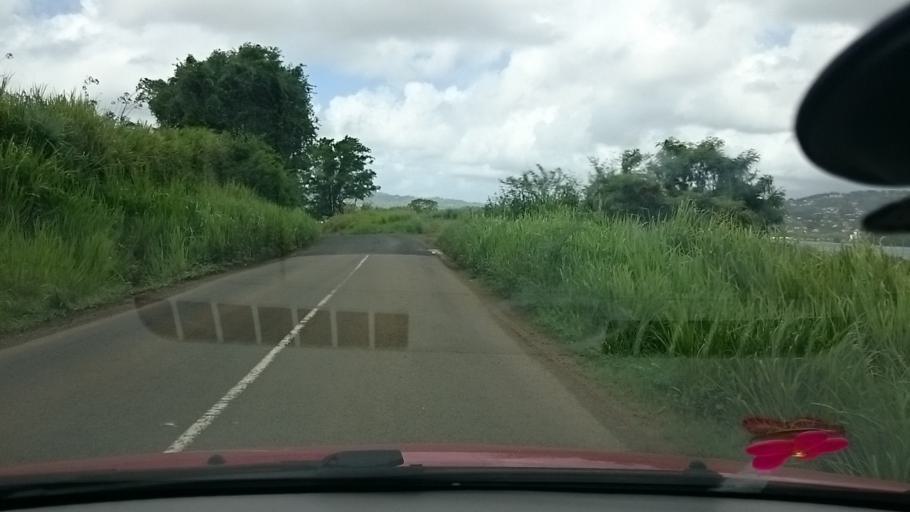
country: MQ
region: Martinique
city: Petite Riviere Salee
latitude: 14.7515
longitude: -60.9434
